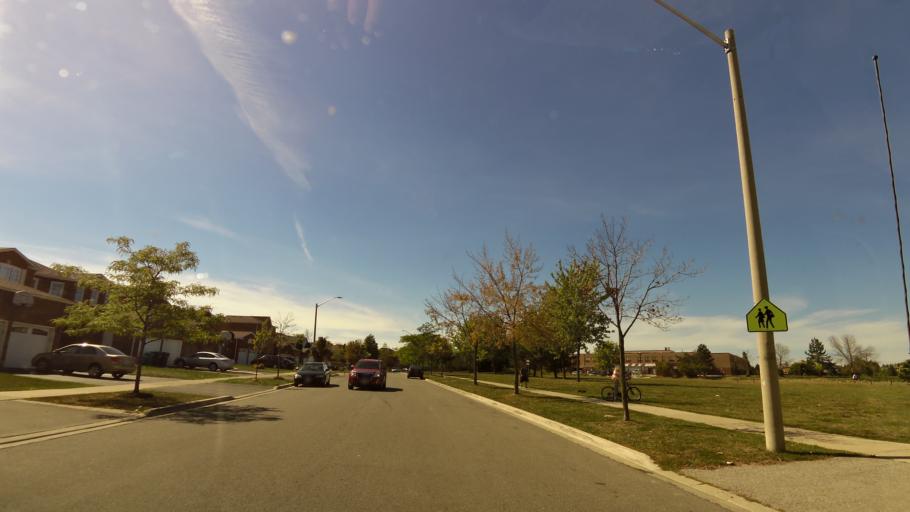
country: CA
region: Ontario
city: Mississauga
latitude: 43.6047
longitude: -79.6636
